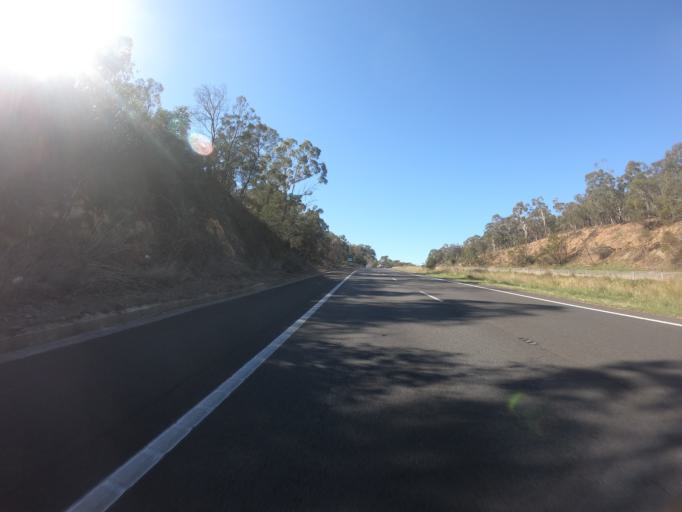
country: AU
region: New South Wales
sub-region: Wingecarribee
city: Bundanoon
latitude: -34.6518
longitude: 150.0901
